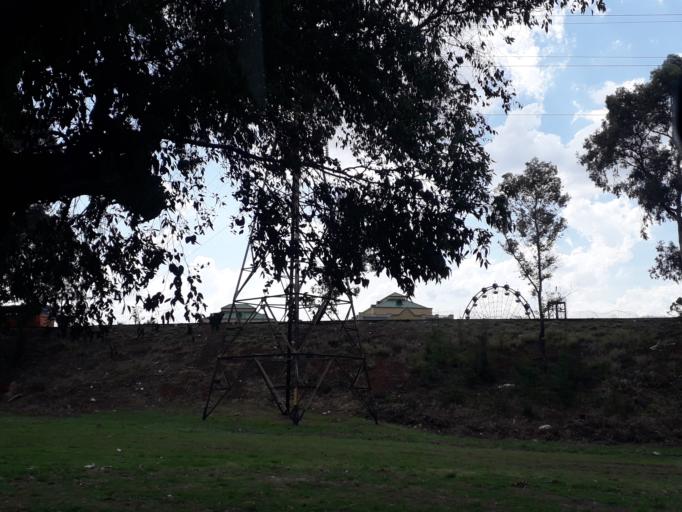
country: ZA
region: Gauteng
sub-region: City of Johannesburg Metropolitan Municipality
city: Johannesburg
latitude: -26.2395
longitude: 28.0159
